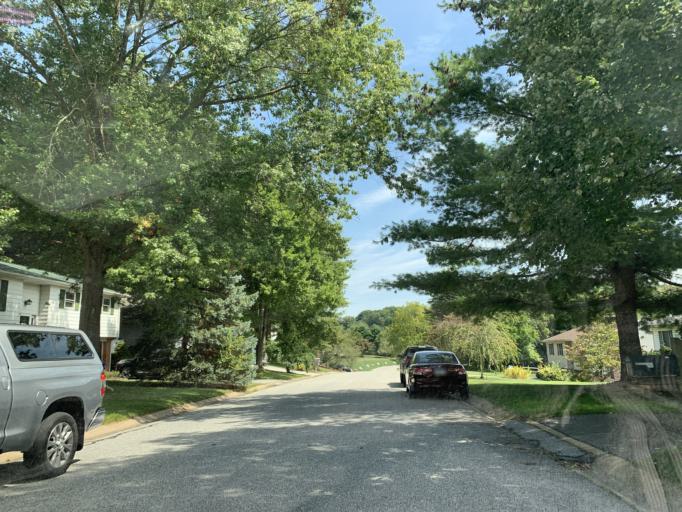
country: US
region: Pennsylvania
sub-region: York County
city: Spry
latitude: 39.9043
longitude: -76.6932
